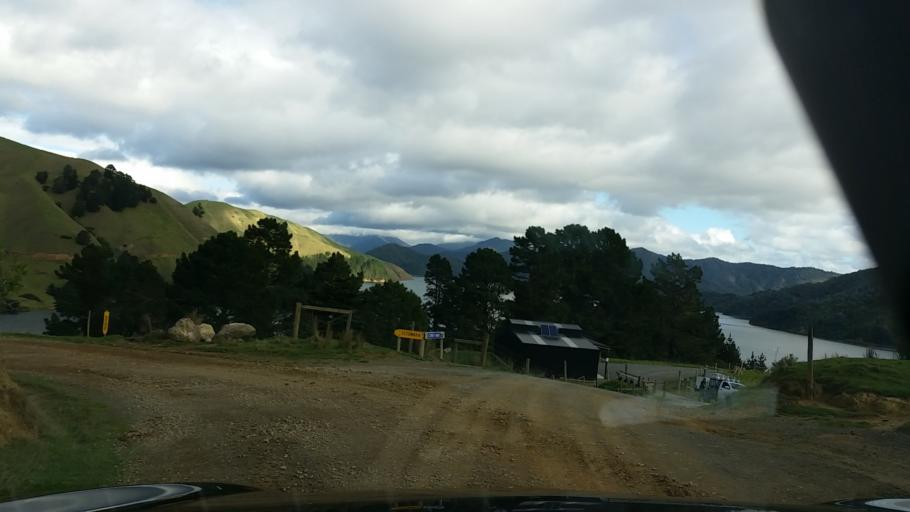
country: NZ
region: Marlborough
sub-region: Marlborough District
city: Picton
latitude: -40.9912
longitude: 173.8317
